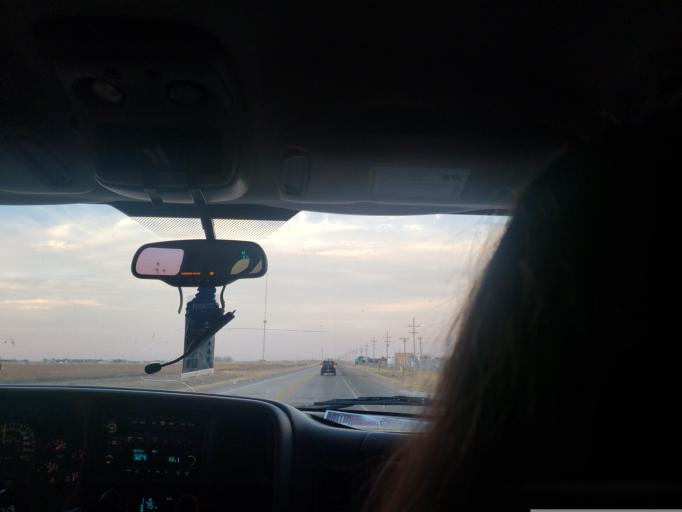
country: US
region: Kansas
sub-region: Seward County
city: Liberal
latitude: 37.0545
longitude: -100.9041
